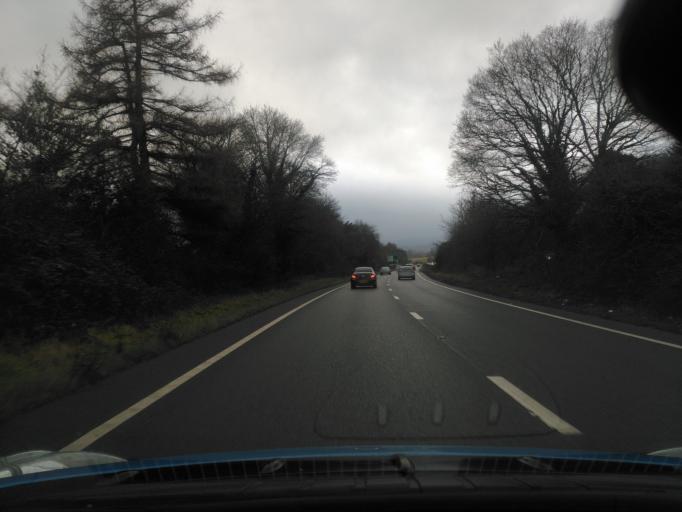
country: GB
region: England
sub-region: Surrey
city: Milford
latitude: 51.1956
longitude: -0.6464
